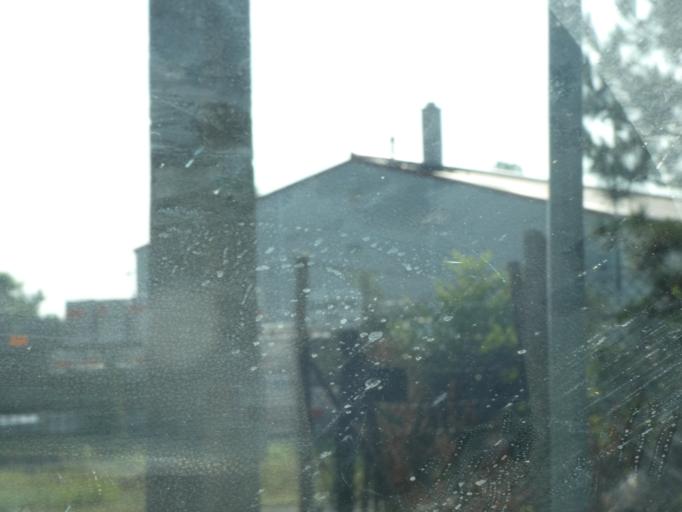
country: HU
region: Pest
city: Orkeny
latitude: 47.1337
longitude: 19.4432
